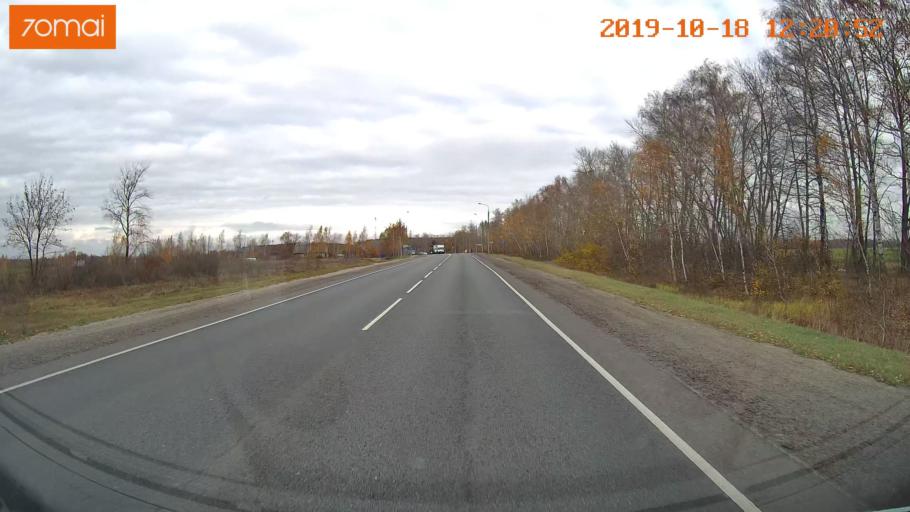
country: RU
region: Rjazan
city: Bagramovo
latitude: 54.5042
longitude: 39.4853
